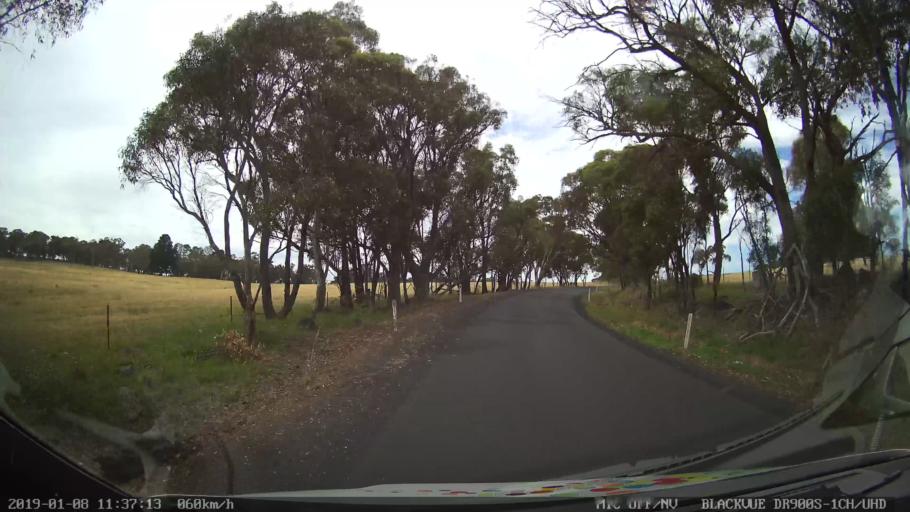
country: AU
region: New South Wales
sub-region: Guyra
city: Guyra
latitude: -30.3507
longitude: 151.5501
